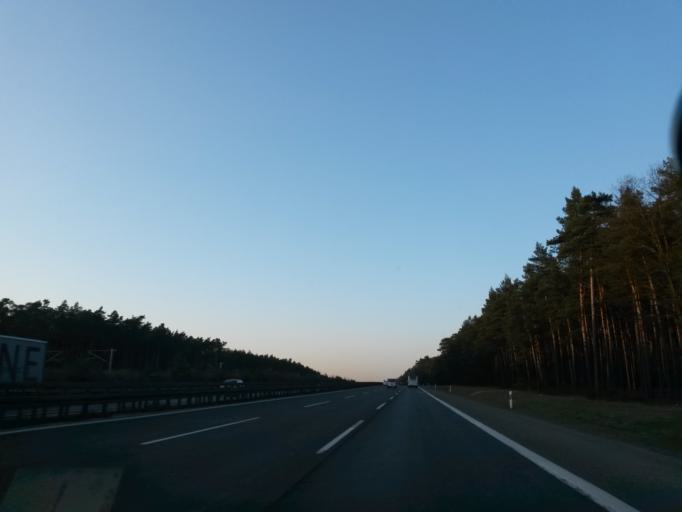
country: DE
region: Bavaria
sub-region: Regierungsbezirk Mittelfranken
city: Schwarzenbruck
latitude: 49.3116
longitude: 11.2079
